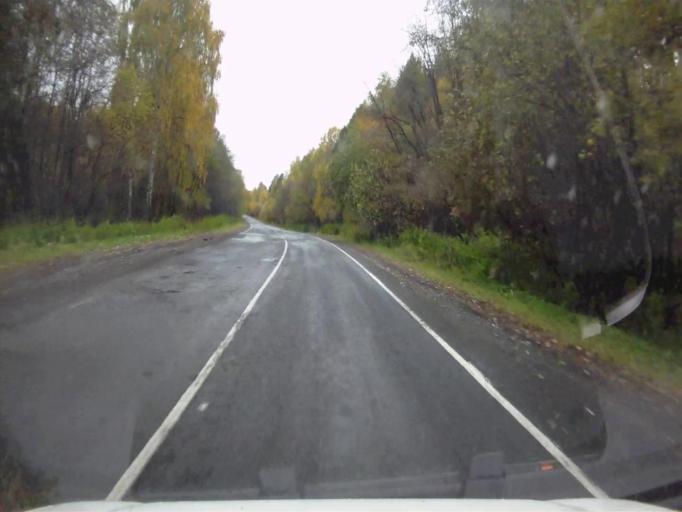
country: RU
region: Chelyabinsk
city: Verkhniy Ufaley
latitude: 56.0468
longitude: 60.1173
